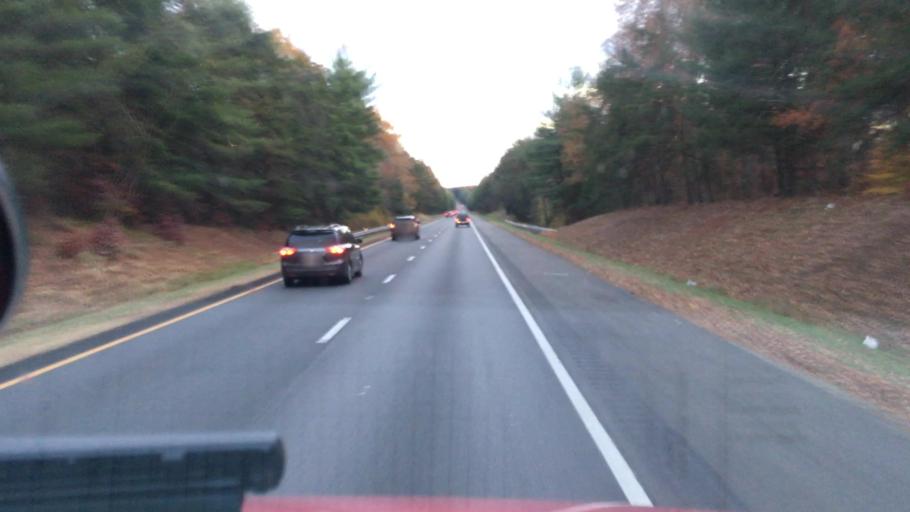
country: US
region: Virginia
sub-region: Fluvanna County
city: Palmyra
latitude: 37.9677
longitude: -78.1915
